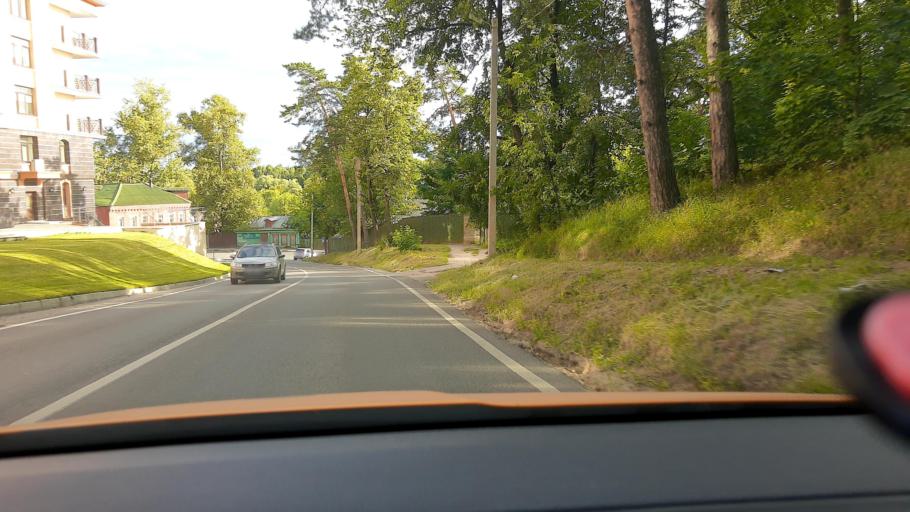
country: RU
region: Moskovskaya
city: Zvenigorod
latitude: 55.7320
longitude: 36.8474
